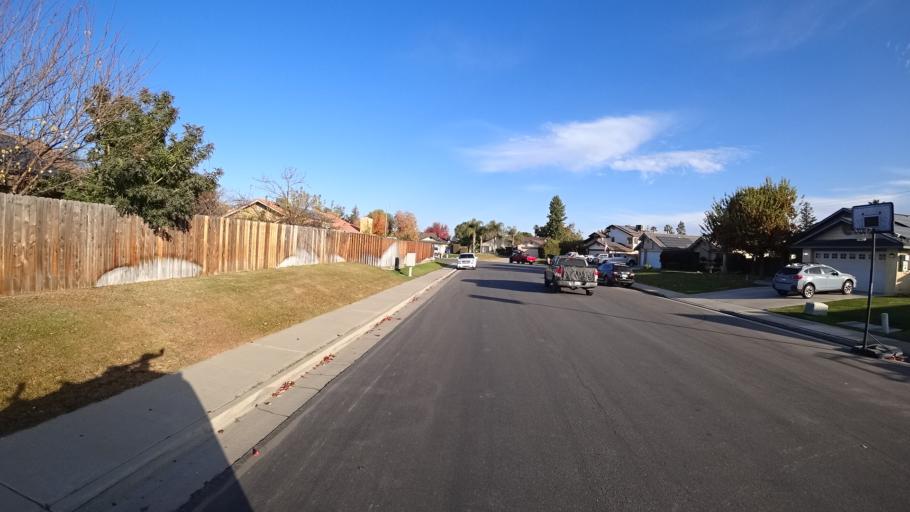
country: US
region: California
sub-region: Kern County
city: Rosedale
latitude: 35.3508
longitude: -119.1551
